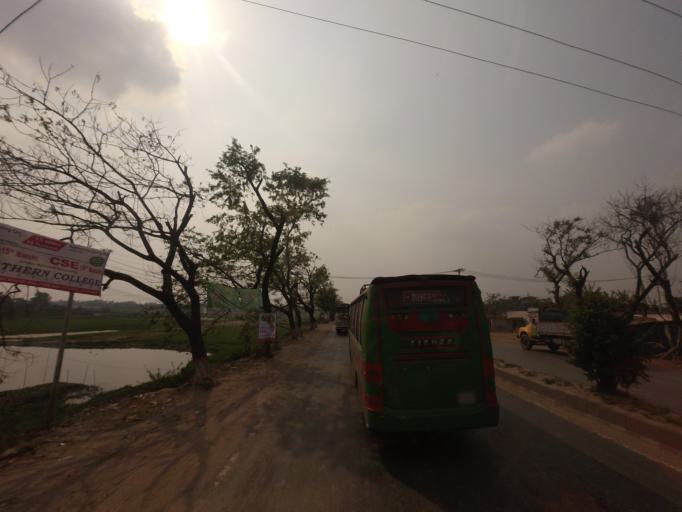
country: BD
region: Dhaka
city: Azimpur
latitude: 23.7902
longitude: 90.3126
